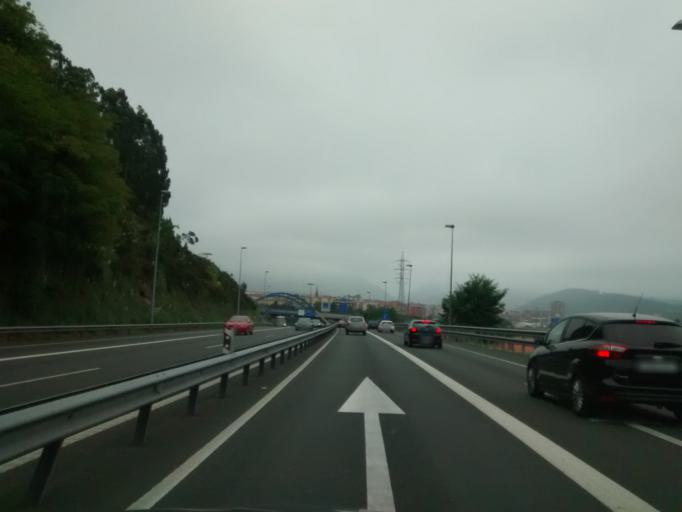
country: ES
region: Cantabria
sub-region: Provincia de Cantabria
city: Torrelavega
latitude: 43.3621
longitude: -4.0439
